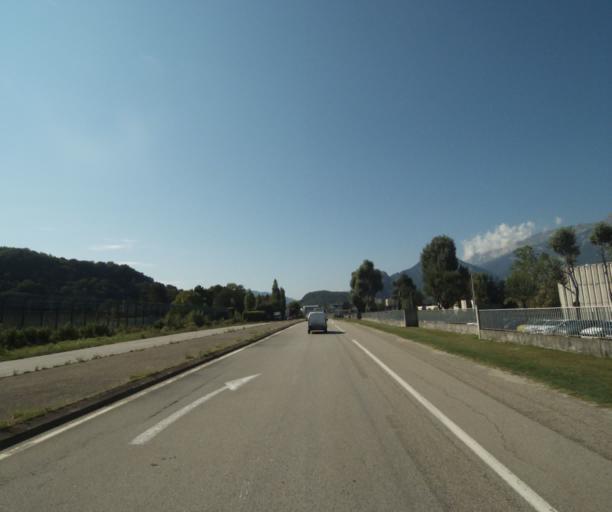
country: FR
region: Rhone-Alpes
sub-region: Departement de l'Isere
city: Allieres-et-Risset
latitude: 45.1008
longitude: 5.6850
